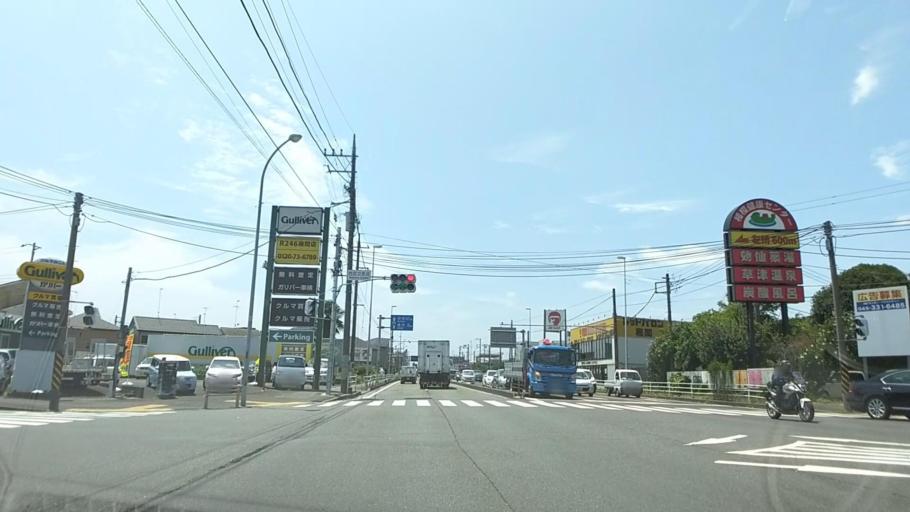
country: JP
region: Kanagawa
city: Zama
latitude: 35.4762
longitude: 139.4155
